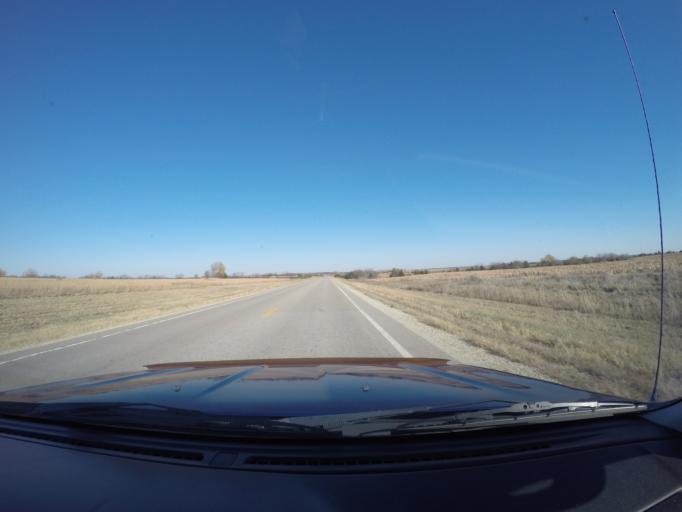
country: US
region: Kansas
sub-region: Riley County
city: Manhattan
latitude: 39.3682
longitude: -96.7565
